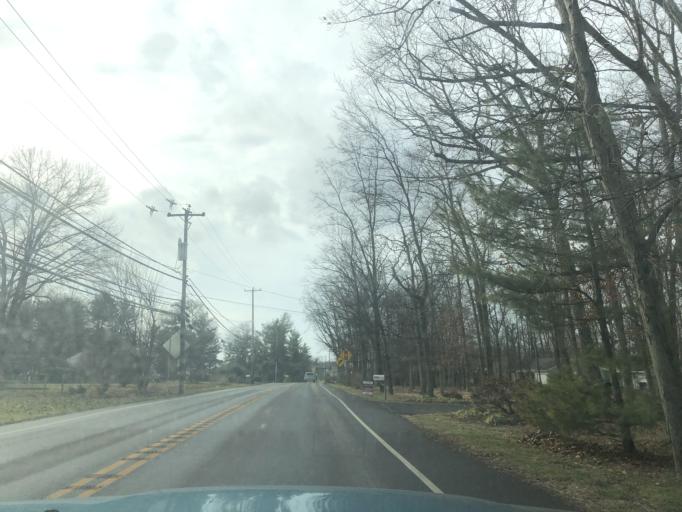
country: US
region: Pennsylvania
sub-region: Montgomery County
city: Harleysville
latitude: 40.2692
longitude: -75.3991
